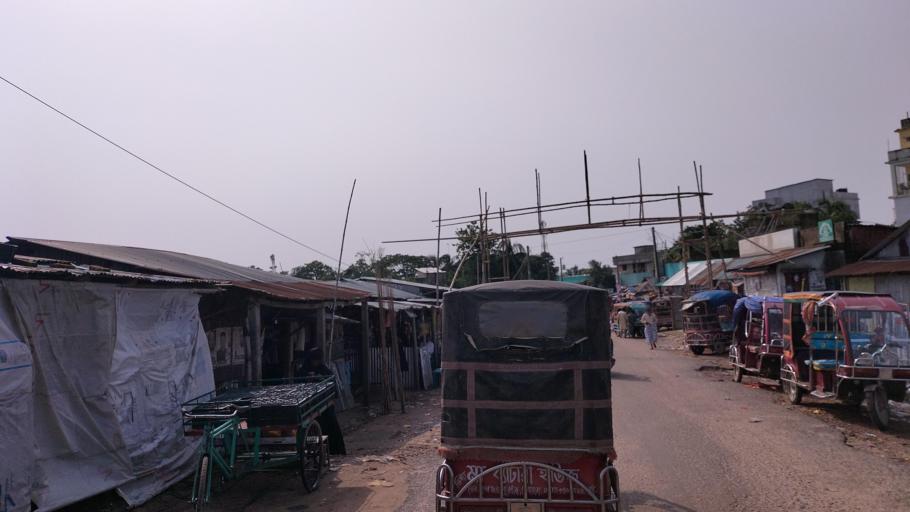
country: BD
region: Dhaka
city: Netrakona
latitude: 25.0760
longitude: 90.8895
